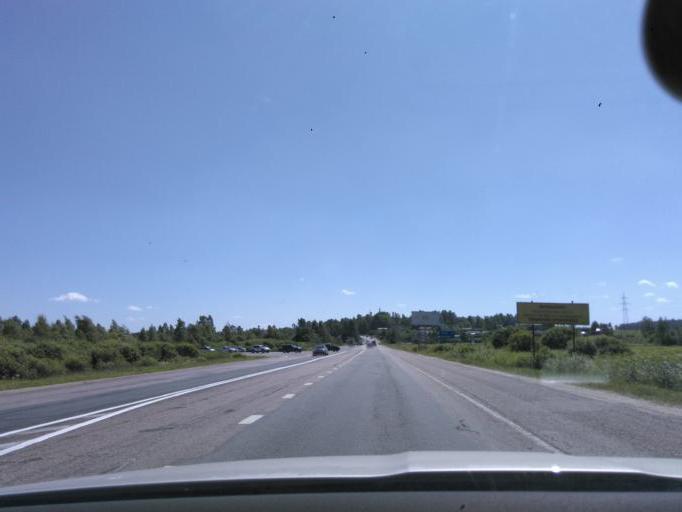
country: RU
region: Moskovskaya
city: Solnechnogorsk
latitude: 56.1554
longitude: 36.9204
